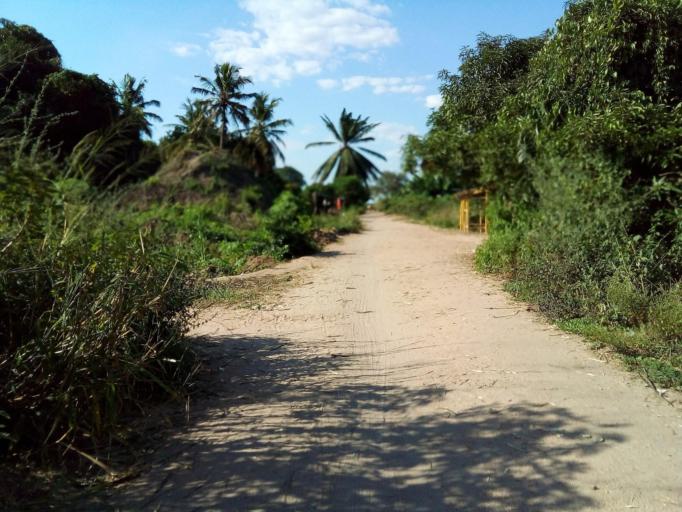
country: MZ
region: Zambezia
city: Quelimane
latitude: -17.5933
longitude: 36.8325
